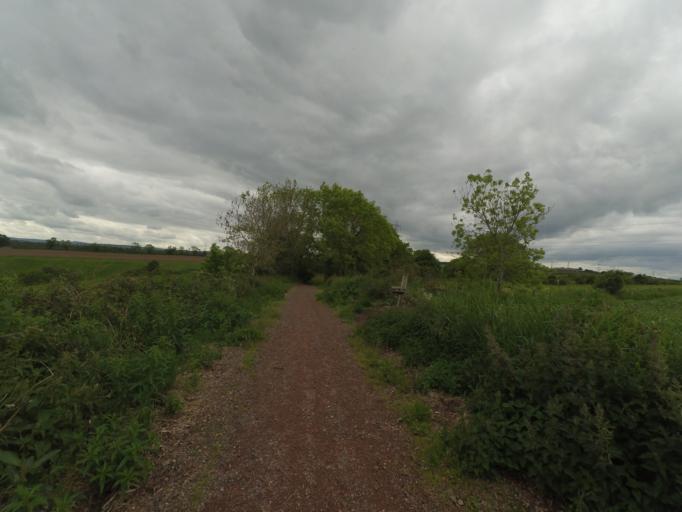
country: GB
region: Scotland
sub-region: East Lothian
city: Ormiston
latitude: 55.9139
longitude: -2.9662
